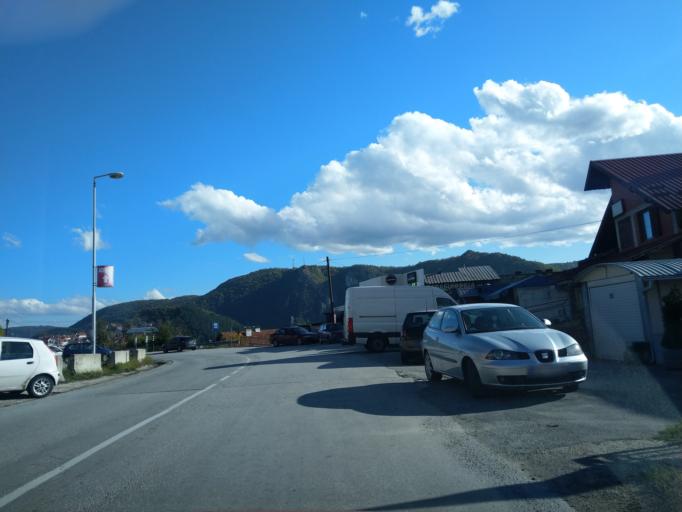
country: RS
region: Central Serbia
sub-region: Zlatiborski Okrug
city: Uzice
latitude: 43.8623
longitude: 19.8166
